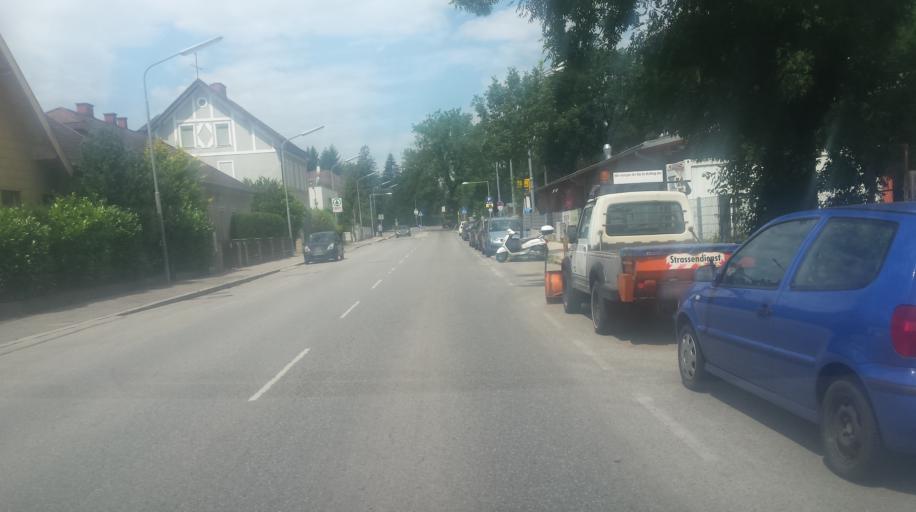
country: AT
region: Lower Austria
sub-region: Politischer Bezirk Wien-Umgebung
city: Purkersdorf
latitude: 48.2291
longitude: 16.2028
